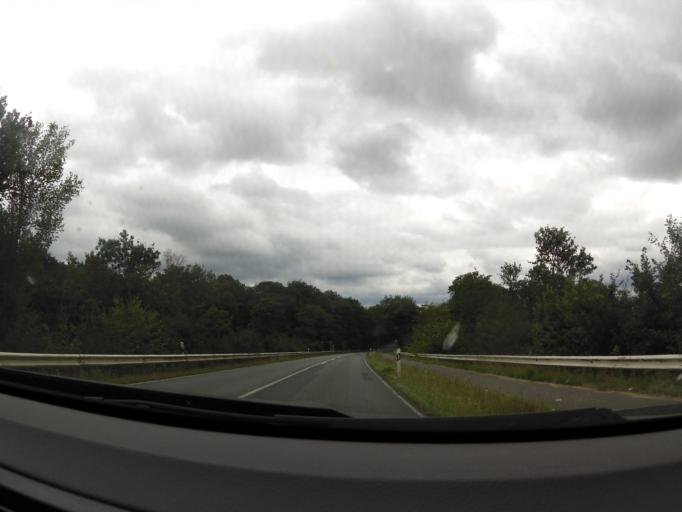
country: DE
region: North Rhine-Westphalia
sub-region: Regierungsbezirk Dusseldorf
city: Alpen
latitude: 51.6199
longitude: 6.4869
